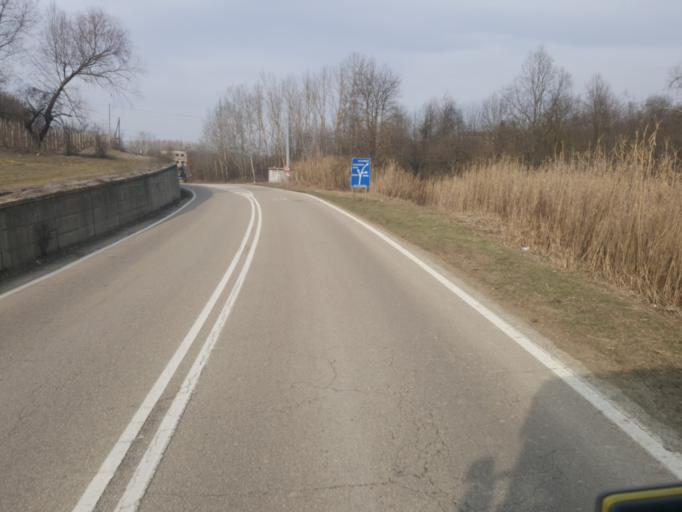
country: IT
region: Piedmont
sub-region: Provincia di Asti
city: Bruno
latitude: 44.7935
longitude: 8.4251
